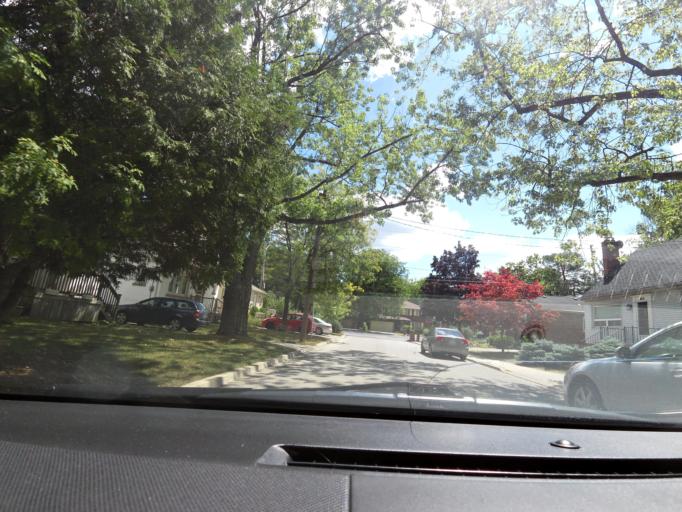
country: CA
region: Ontario
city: Burlington
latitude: 43.3312
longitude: -79.7941
